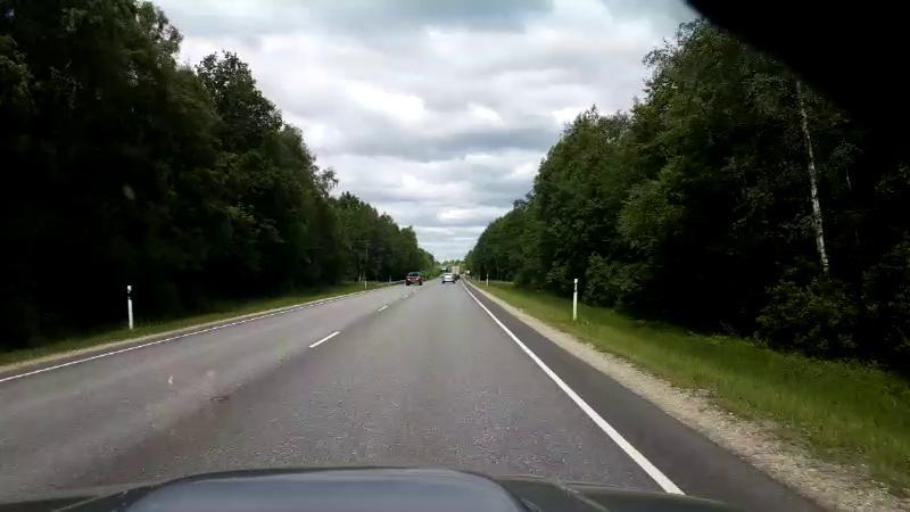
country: EE
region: Paernumaa
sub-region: Halinga vald
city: Parnu-Jaagupi
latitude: 58.6096
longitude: 24.5124
